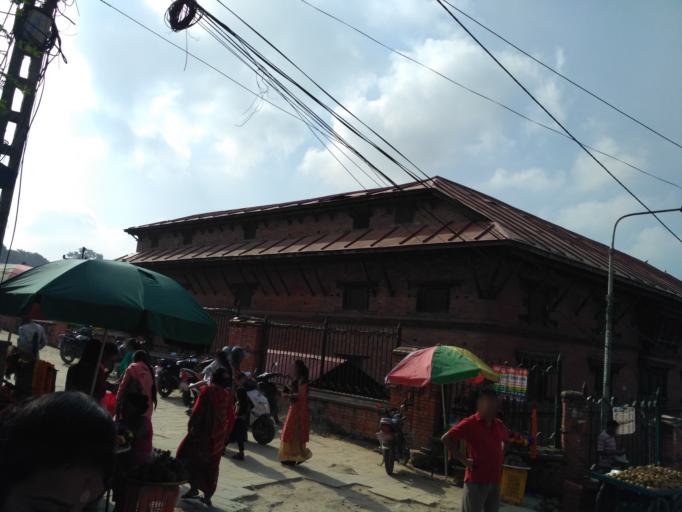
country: NP
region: Central Region
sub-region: Bagmati Zone
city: Kathmandu
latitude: 27.7114
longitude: 85.3472
